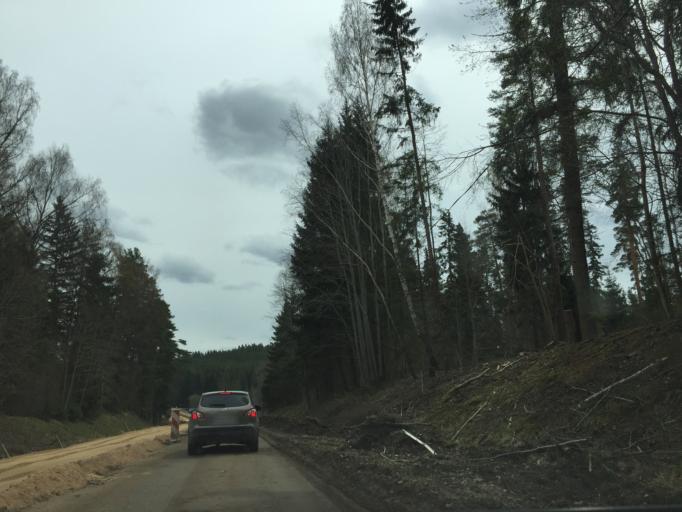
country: LV
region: Priekuli
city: Priekuli
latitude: 57.3111
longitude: 25.3827
